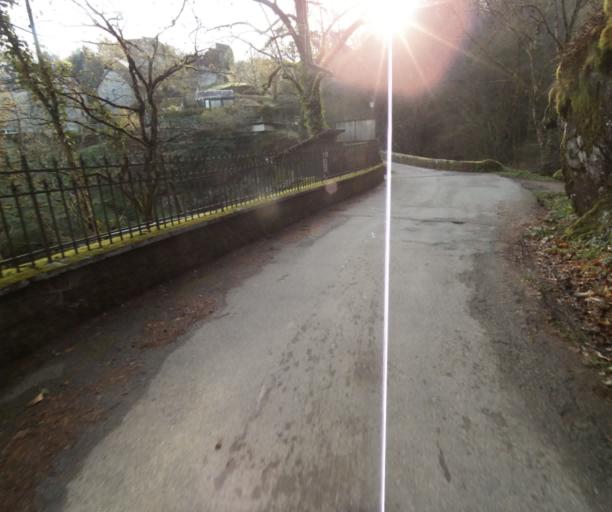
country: FR
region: Limousin
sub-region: Departement de la Correze
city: Correze
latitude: 45.2980
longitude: 1.8502
